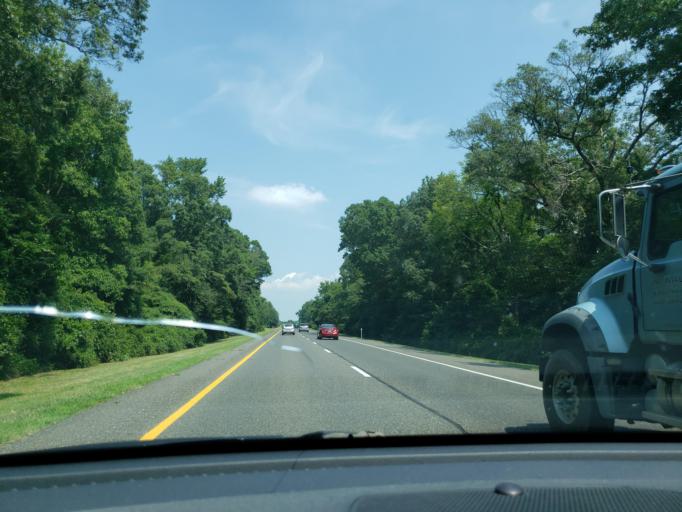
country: US
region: New Jersey
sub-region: Cape May County
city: Erma
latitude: 38.9756
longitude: -74.8920
